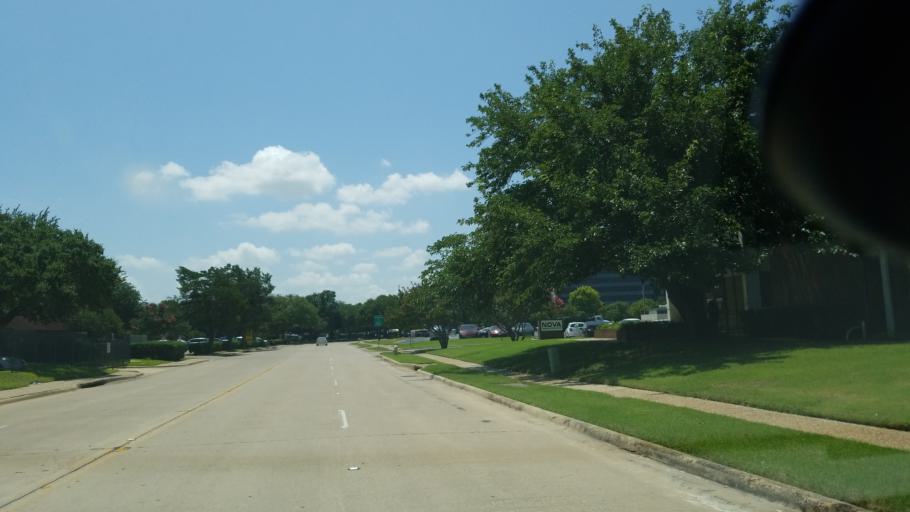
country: US
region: Texas
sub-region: Dallas County
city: University Park
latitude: 32.8243
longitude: -96.8655
